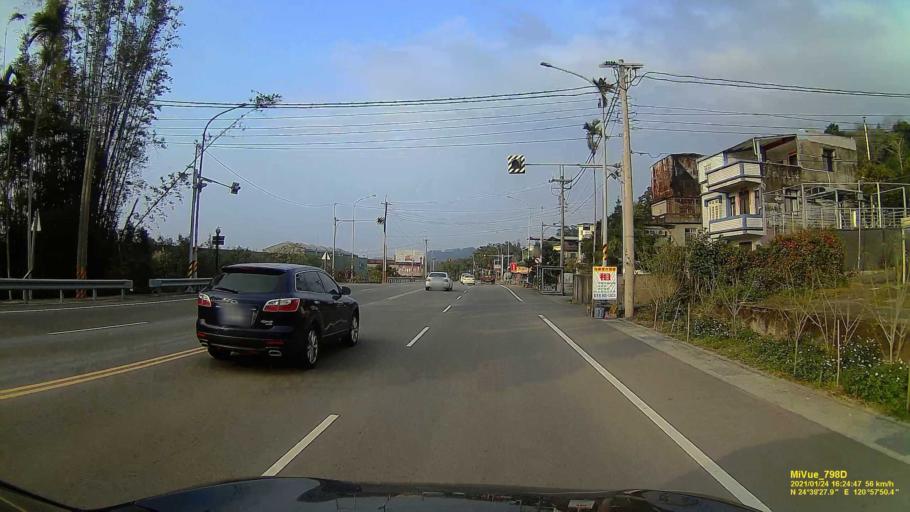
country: TW
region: Taiwan
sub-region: Hsinchu
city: Hsinchu
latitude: 24.6582
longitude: 120.9642
